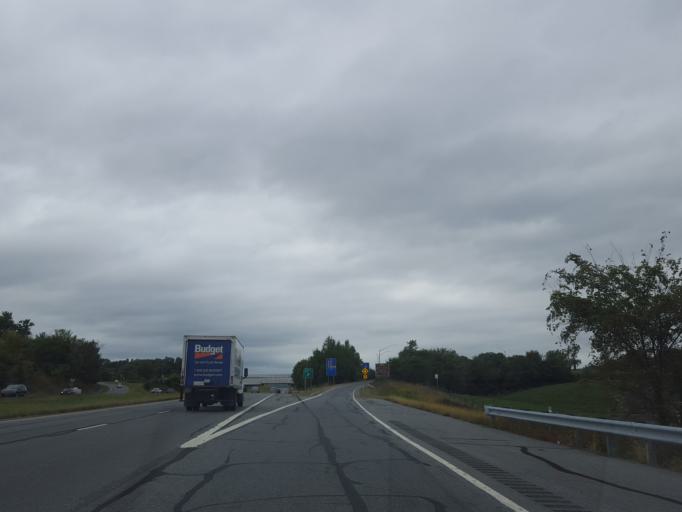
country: US
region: Maryland
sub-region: Frederick County
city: Brunswick
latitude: 39.3418
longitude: -77.6374
